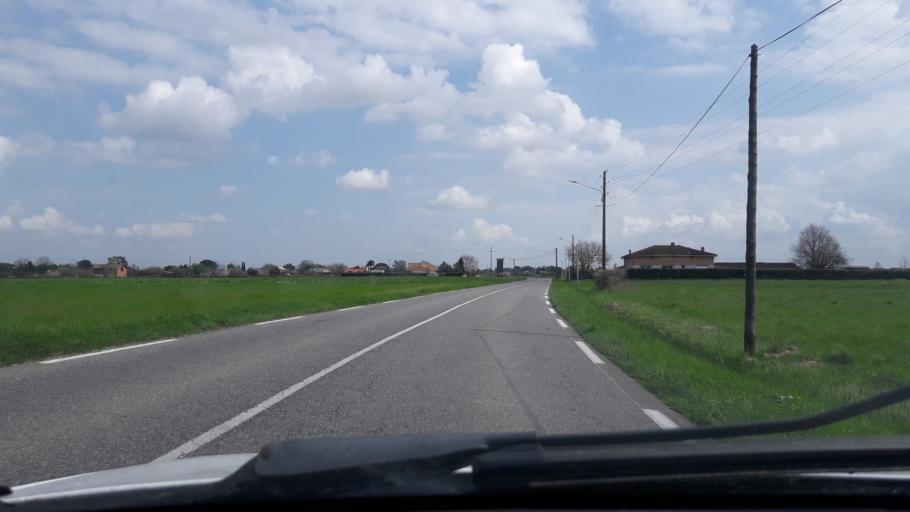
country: FR
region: Midi-Pyrenees
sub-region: Departement de la Haute-Garonne
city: Seysses
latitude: 43.5010
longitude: 1.2827
